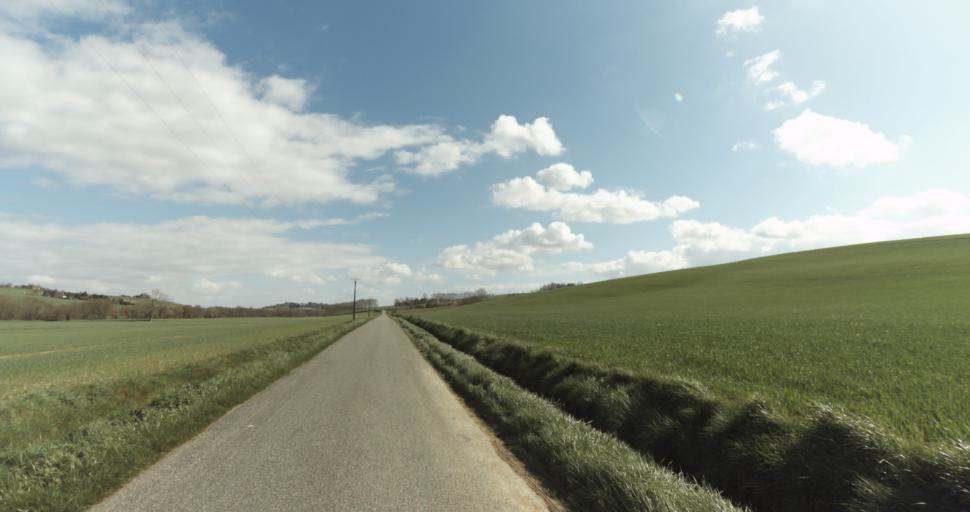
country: FR
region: Midi-Pyrenees
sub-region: Departement de la Haute-Garonne
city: Auterive
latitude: 43.3680
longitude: 1.5204
